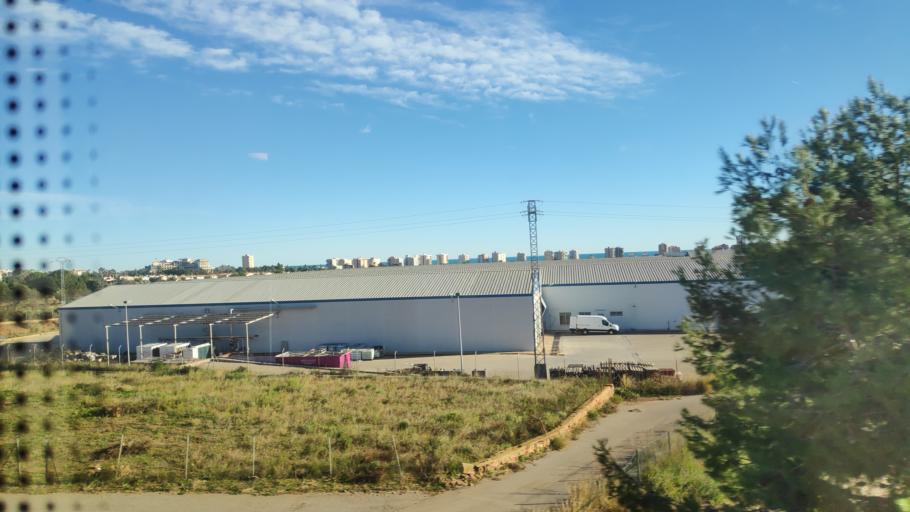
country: ES
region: Valencia
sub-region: Provincia de Castello
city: Benicassim
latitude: 40.0447
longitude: 0.0388
